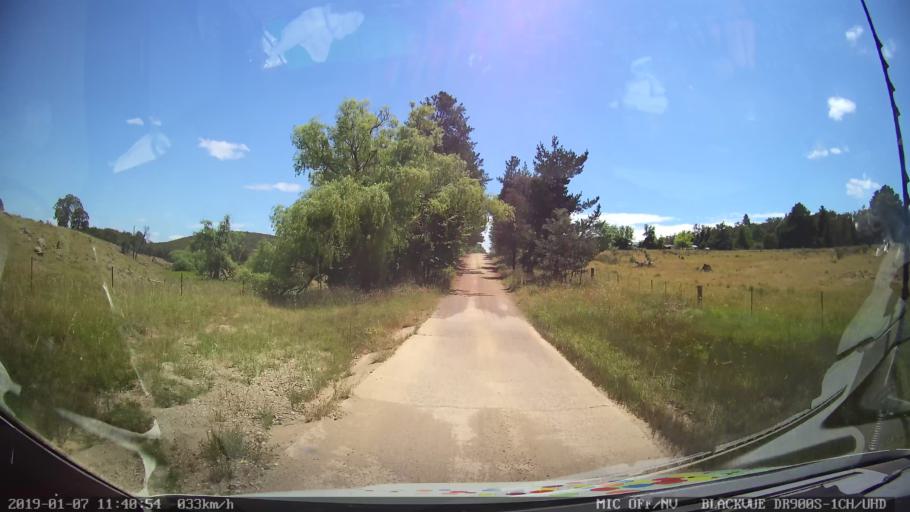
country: AU
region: New South Wales
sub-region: Armidale Dumaresq
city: Armidale
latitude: -30.3629
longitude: 151.5868
